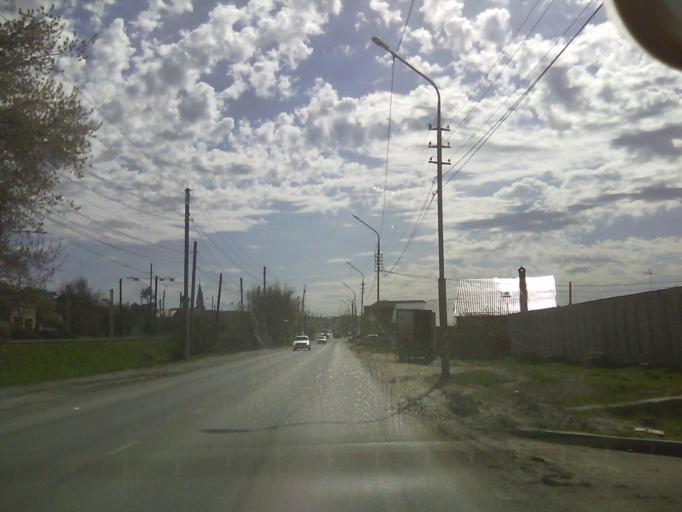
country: RU
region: Saratov
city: Sokolovyy
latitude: 51.5850
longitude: 45.9040
